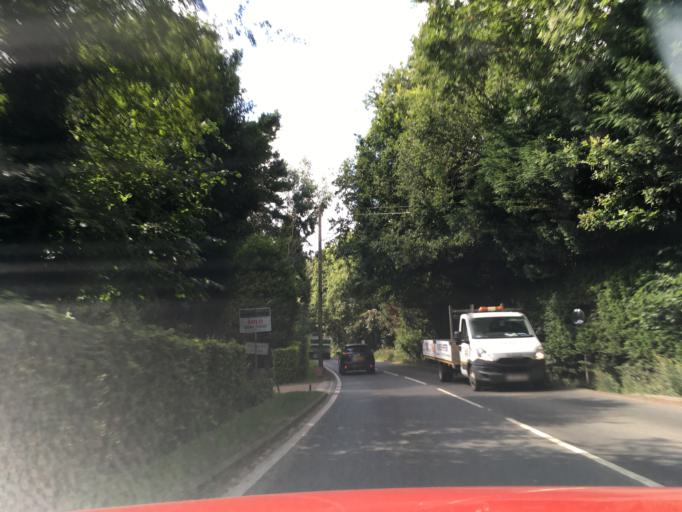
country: GB
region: England
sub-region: Kent
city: Cranbrook
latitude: 51.1229
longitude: 0.5588
